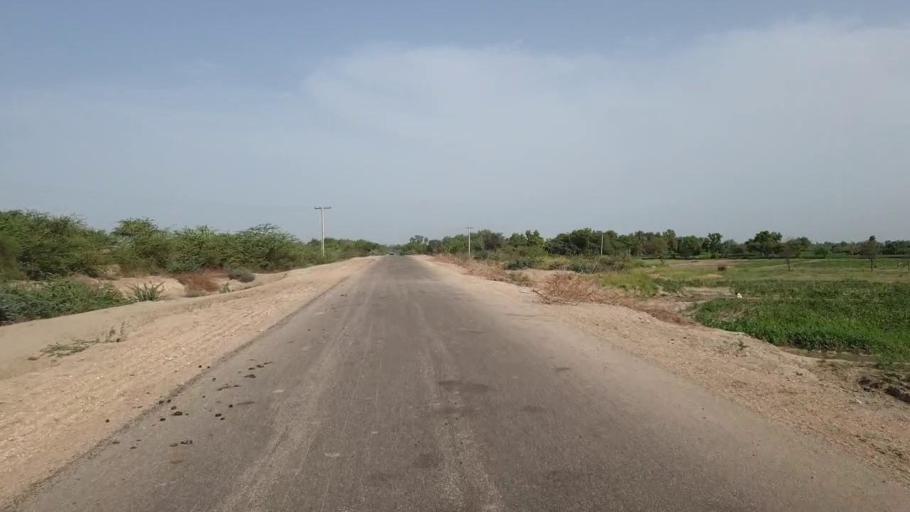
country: PK
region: Sindh
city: Sakrand
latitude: 26.2695
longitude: 68.2779
